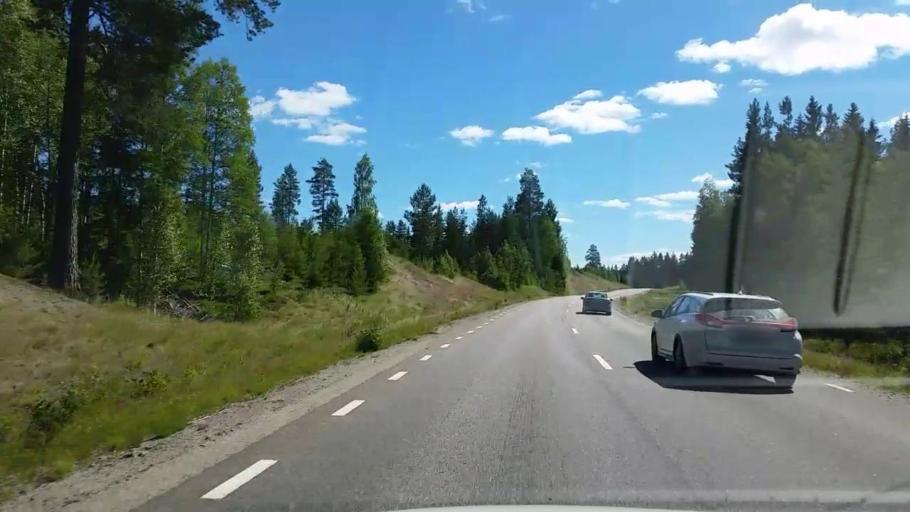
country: SE
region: Gaevleborg
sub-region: Ovanakers Kommun
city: Edsbyn
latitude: 61.1907
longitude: 15.8758
